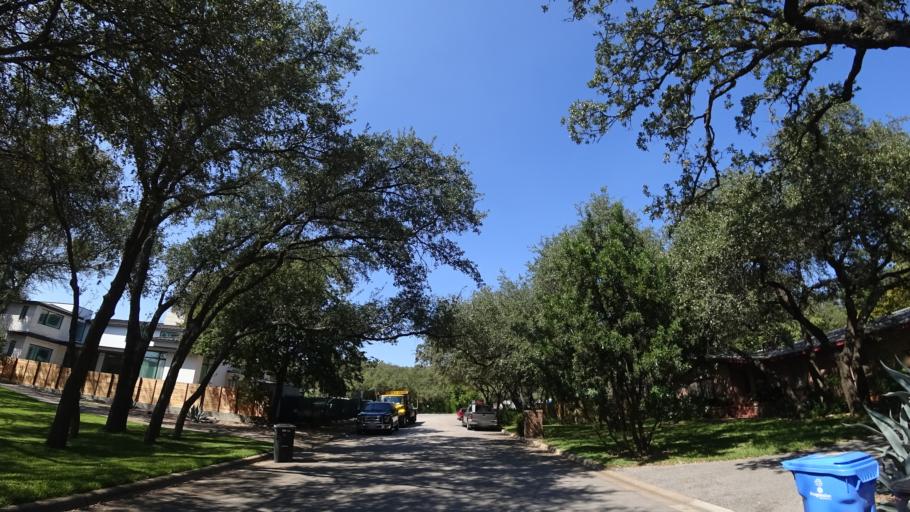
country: US
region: Texas
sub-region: Travis County
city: Rollingwood
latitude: 30.2768
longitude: -97.7904
